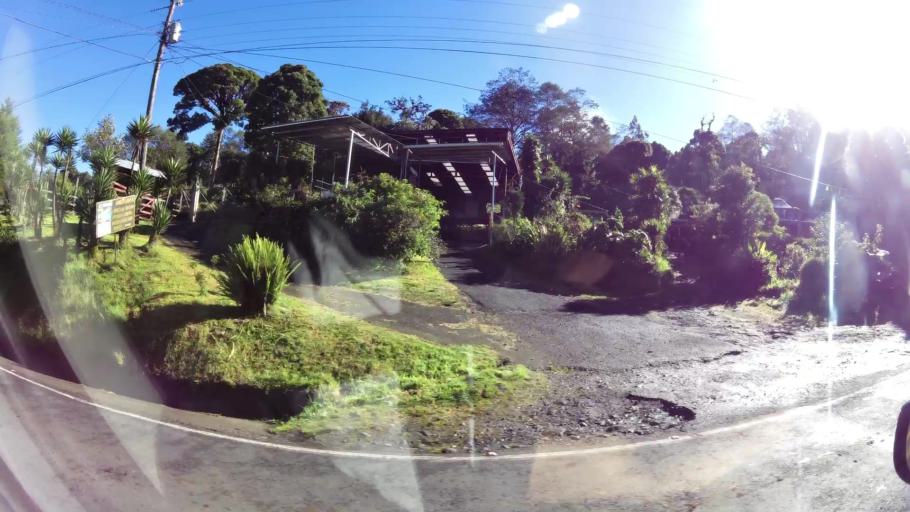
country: CR
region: San Jose
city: San Marcos
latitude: 9.7169
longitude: -83.9493
